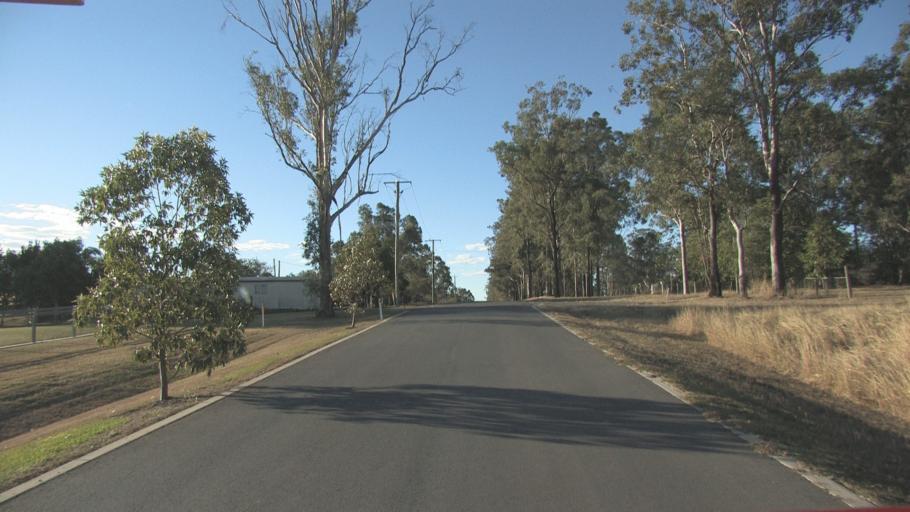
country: AU
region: Queensland
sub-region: Logan
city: Cedar Vale
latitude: -27.8729
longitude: 152.9745
